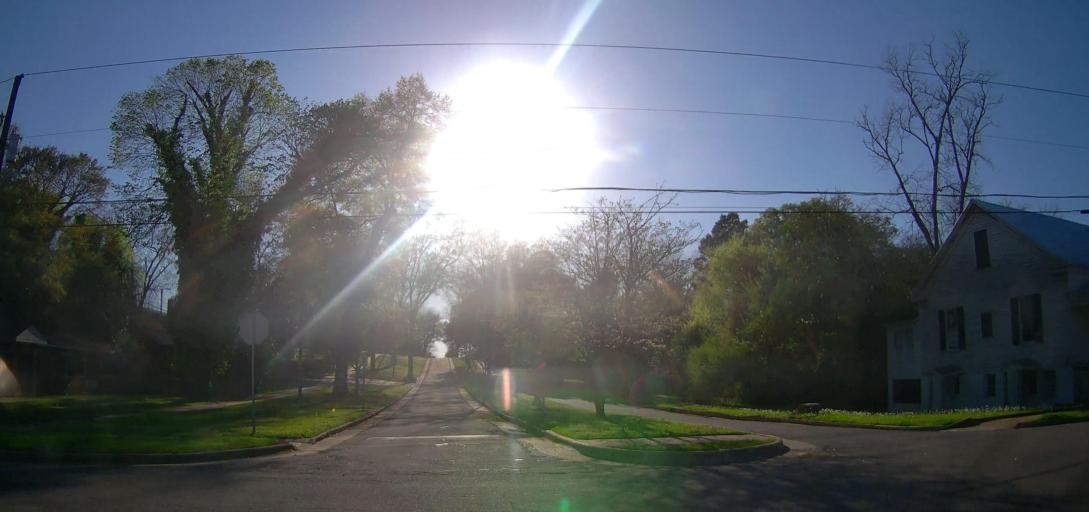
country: US
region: Georgia
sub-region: Baldwin County
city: Milledgeville
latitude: 33.0782
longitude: -83.2282
